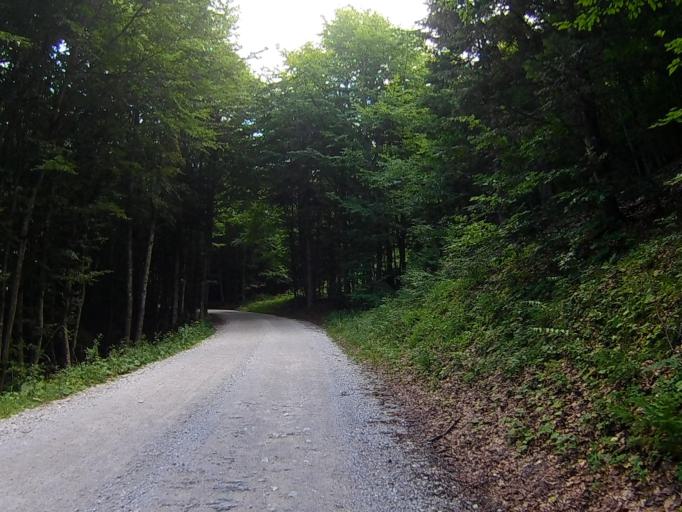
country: SI
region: Ruse
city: Ruse
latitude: 46.4997
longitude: 15.4855
